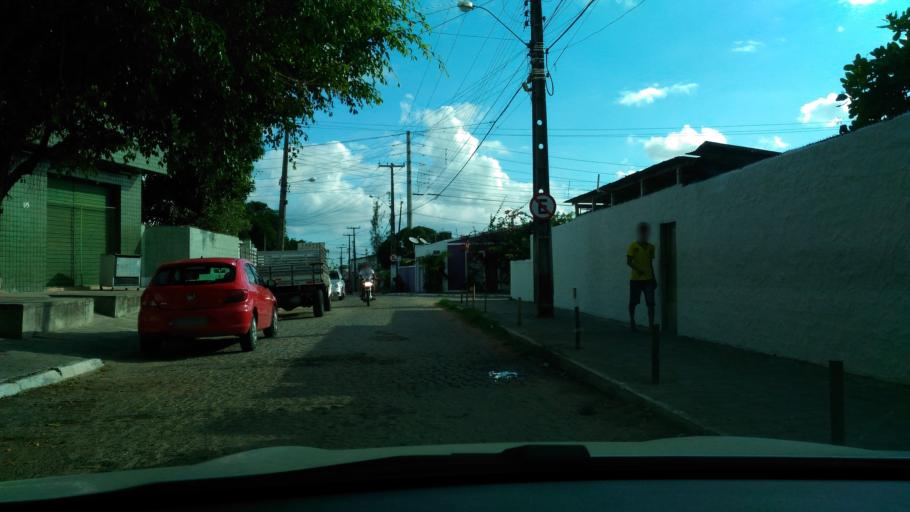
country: BR
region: Paraiba
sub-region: Joao Pessoa
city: Joao Pessoa
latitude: -7.1249
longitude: -34.8864
